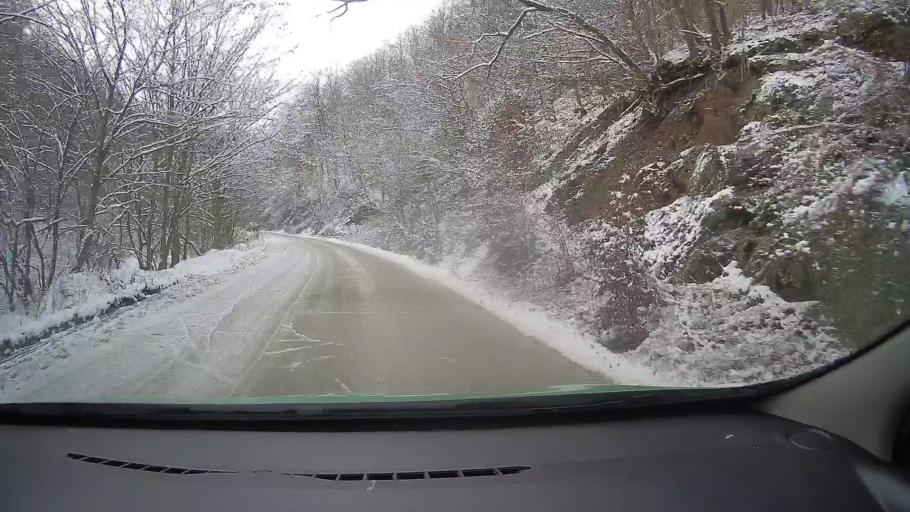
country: RO
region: Alba
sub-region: Oras Zlatna
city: Zlatna
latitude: 46.0990
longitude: 23.1863
